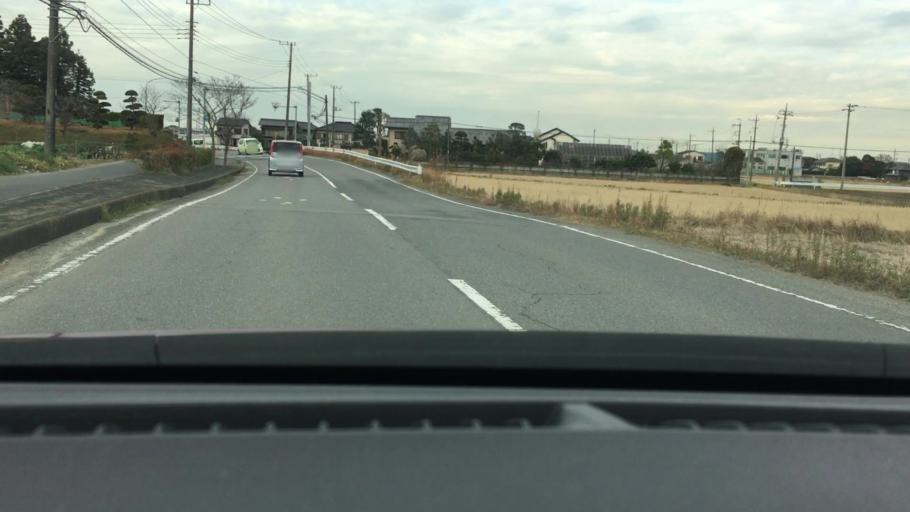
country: JP
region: Chiba
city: Ichihara
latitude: 35.4747
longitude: 140.0630
